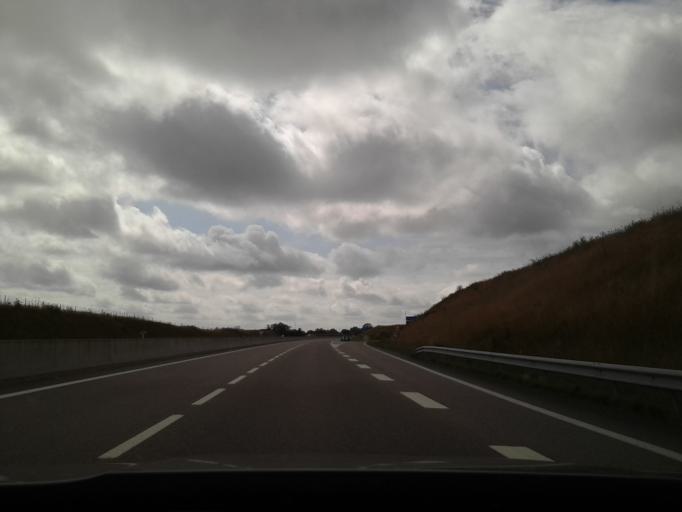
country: FR
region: Lower Normandy
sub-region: Departement de l'Orne
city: Courteilles
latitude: 48.8264
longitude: -0.1388
